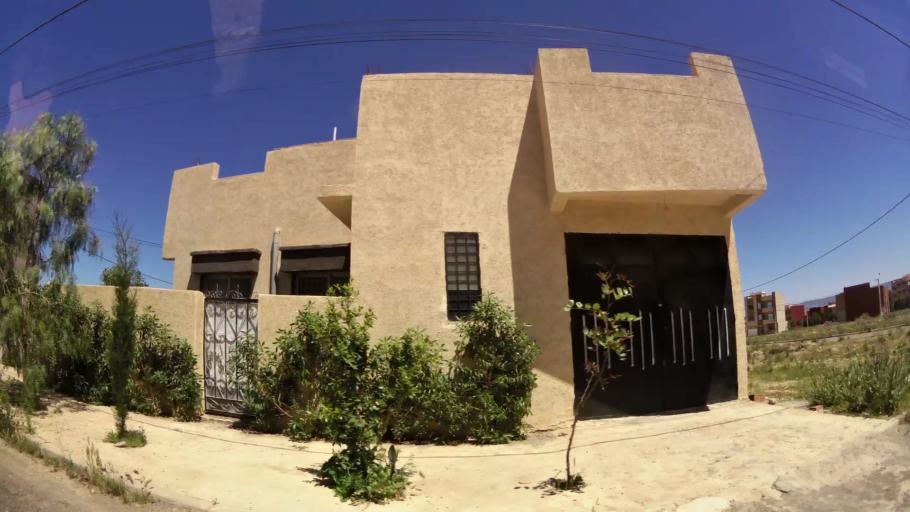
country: MA
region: Oriental
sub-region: Oujda-Angad
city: Oujda
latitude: 34.6843
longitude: -1.8670
